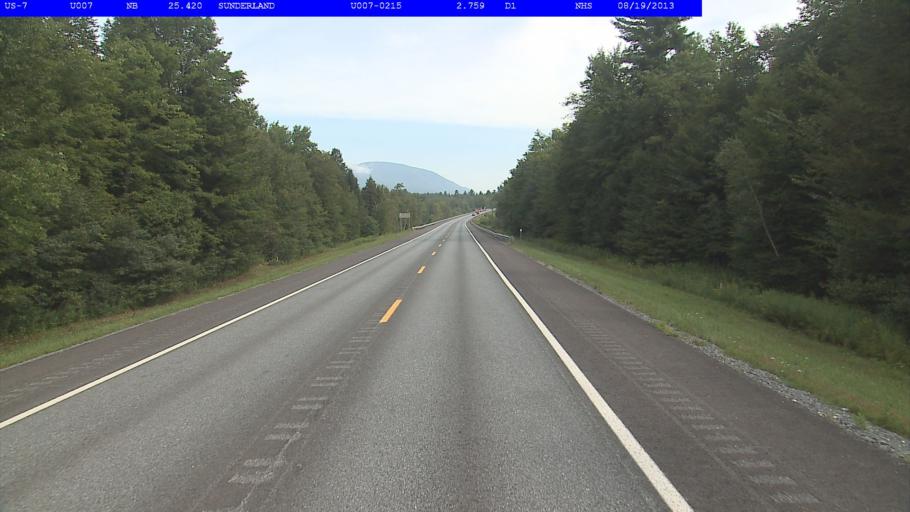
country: US
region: Vermont
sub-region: Bennington County
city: Arlington
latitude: 43.0639
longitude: -73.1243
